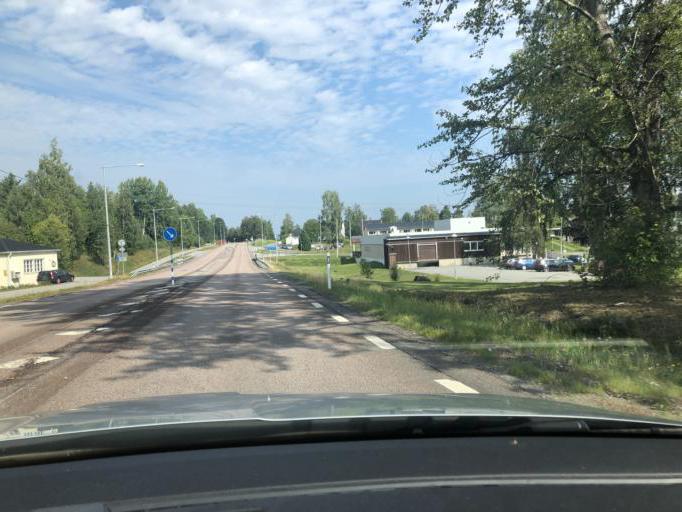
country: SE
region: Vaesternorrland
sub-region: Kramfors Kommun
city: Kramfors
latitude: 62.8063
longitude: 17.8666
